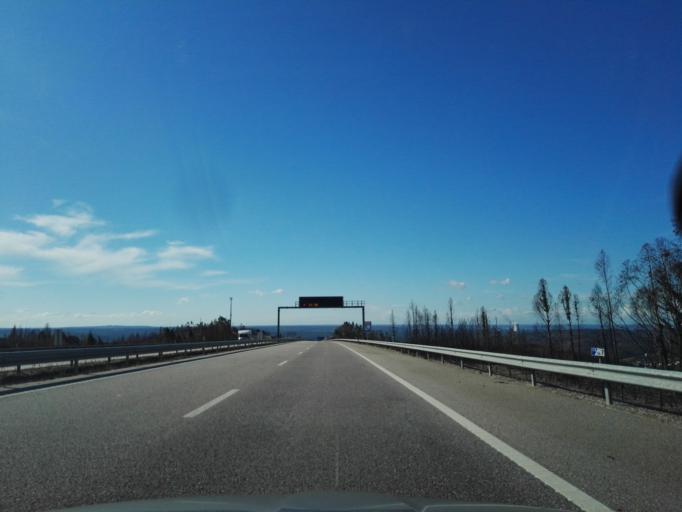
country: PT
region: Santarem
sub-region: Macao
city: Macao
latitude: 39.5095
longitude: -8.0189
